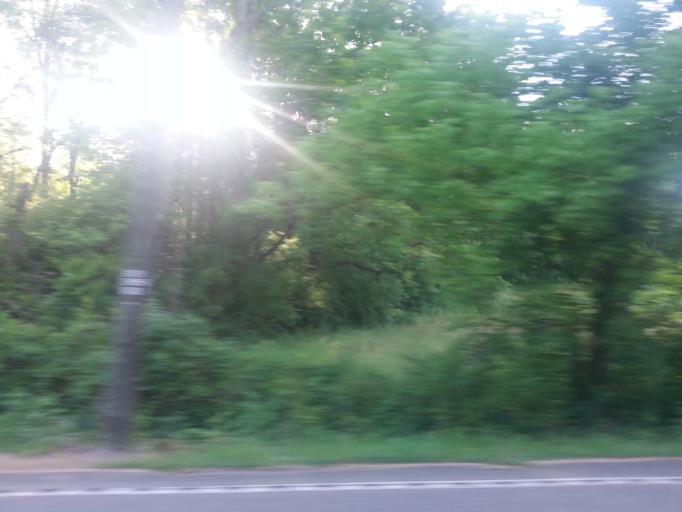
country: US
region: Tennessee
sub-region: Knox County
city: Knoxville
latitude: 35.9112
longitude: -83.9014
